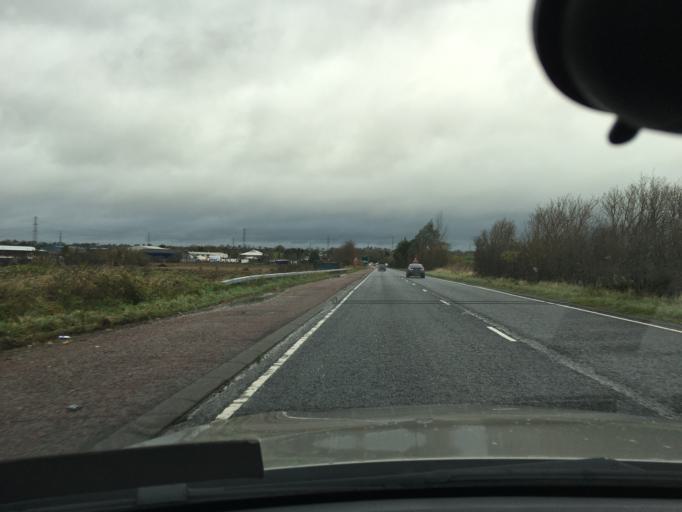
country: GB
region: Northern Ireland
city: Carnmoney
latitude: 54.6989
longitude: -5.9692
